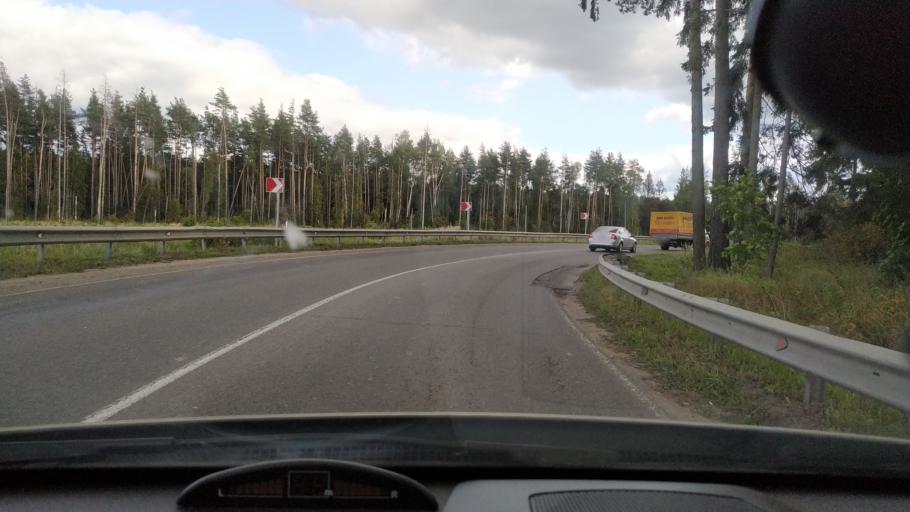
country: RU
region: Moskovskaya
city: Chornaya
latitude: 55.7693
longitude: 38.0562
